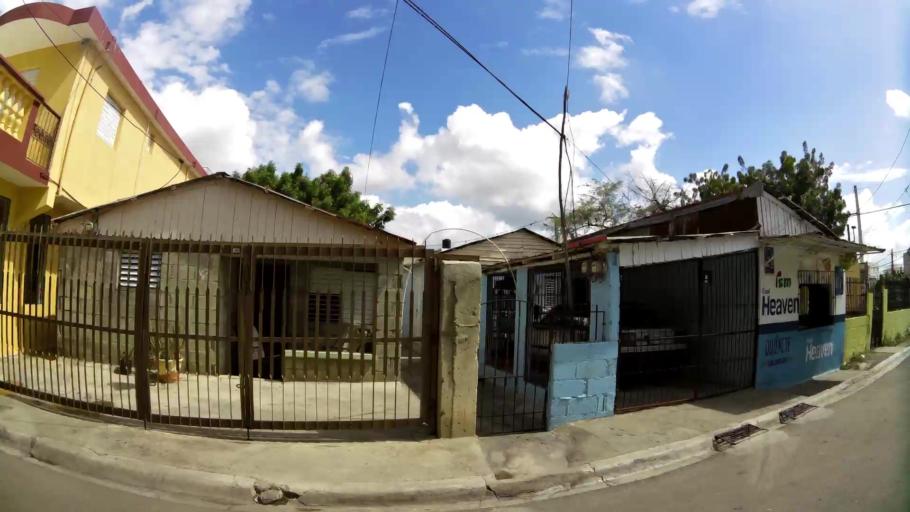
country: DO
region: Santiago
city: Santiago de los Caballeros
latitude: 19.4724
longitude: -70.7008
